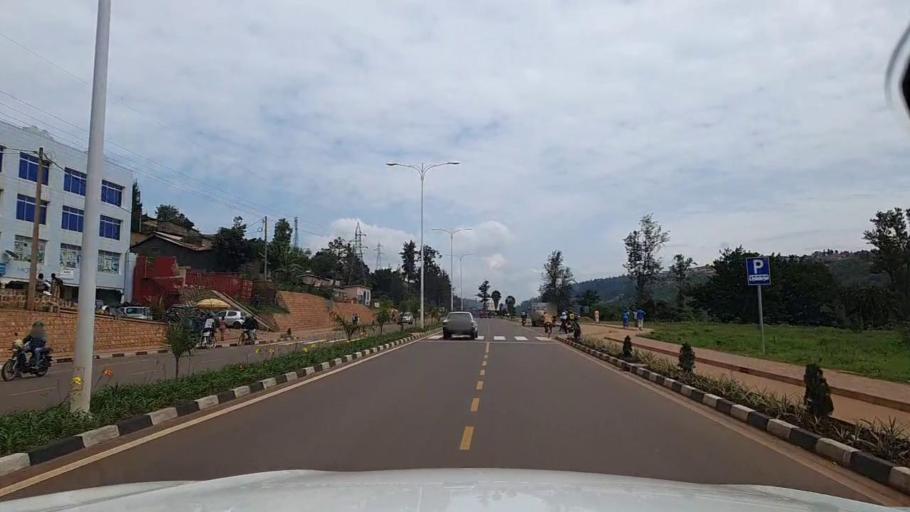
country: RW
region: Kigali
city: Kigali
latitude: -1.9350
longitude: 30.0450
